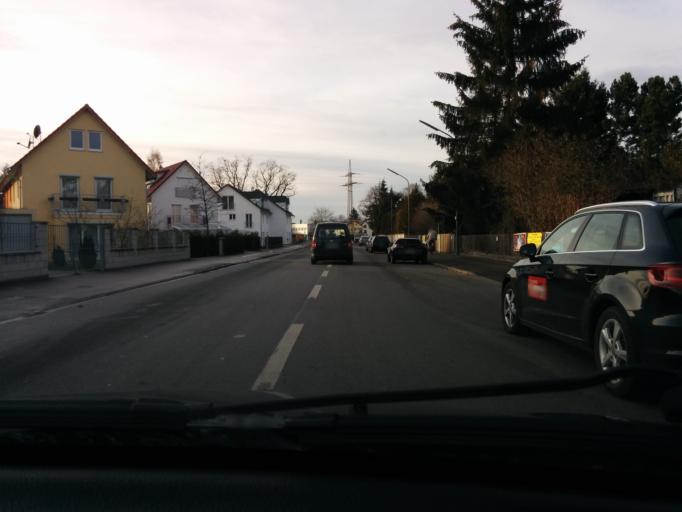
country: DE
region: Bavaria
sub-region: Upper Bavaria
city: Pasing
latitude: 48.1520
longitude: 11.4305
